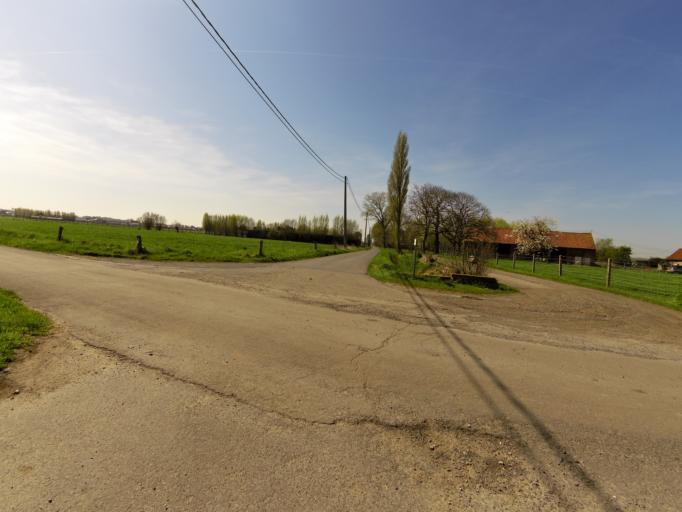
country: BE
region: Flanders
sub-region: Provincie West-Vlaanderen
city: Ichtegem
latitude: 51.1294
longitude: 3.0015
